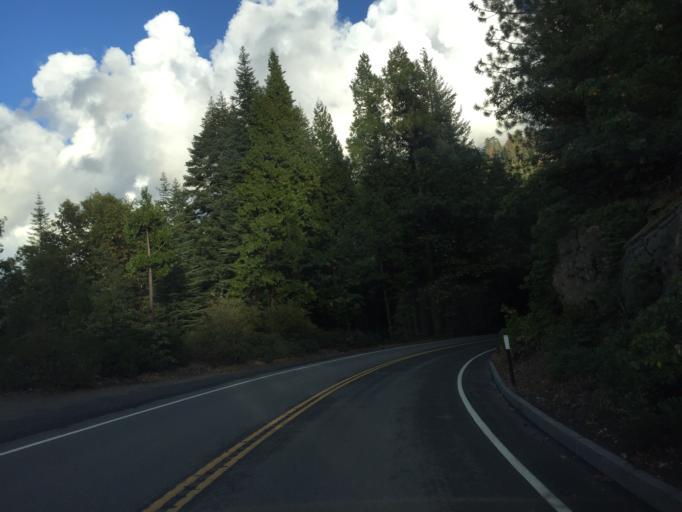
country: US
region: California
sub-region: Madera County
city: Ahwahnee
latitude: 37.5145
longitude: -119.6334
